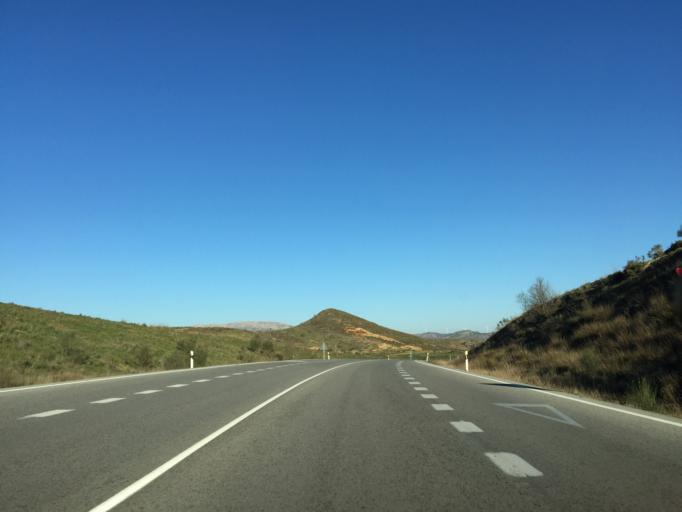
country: ES
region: Andalusia
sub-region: Provincia de Malaga
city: Ardales
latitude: 36.8622
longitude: -4.8398
